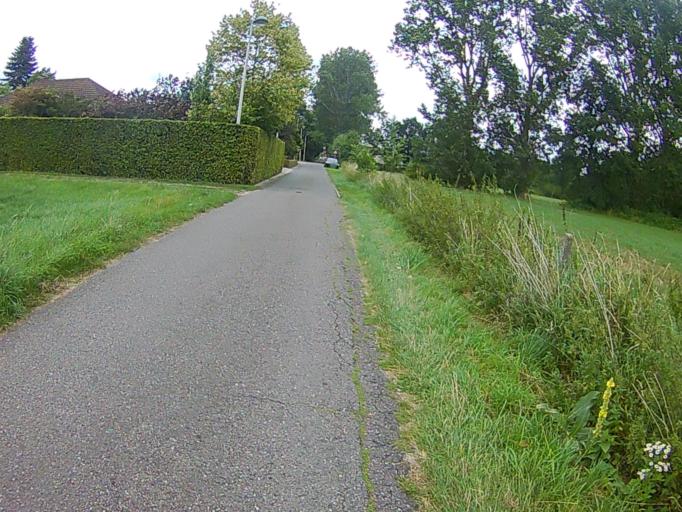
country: BE
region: Flanders
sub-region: Provincie Antwerpen
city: Ranst
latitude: 51.1773
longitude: 4.5880
